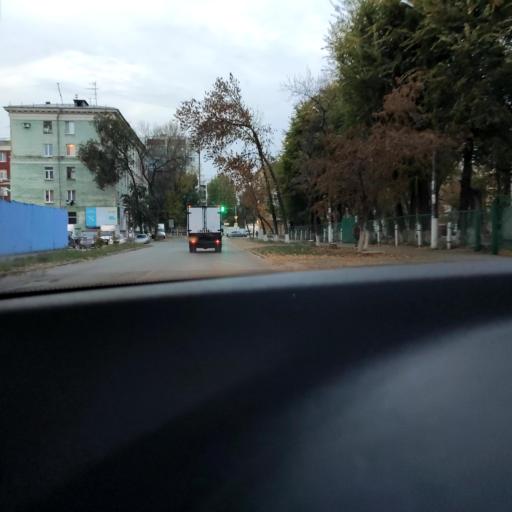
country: RU
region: Samara
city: Petra-Dubrava
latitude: 53.2246
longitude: 50.2778
